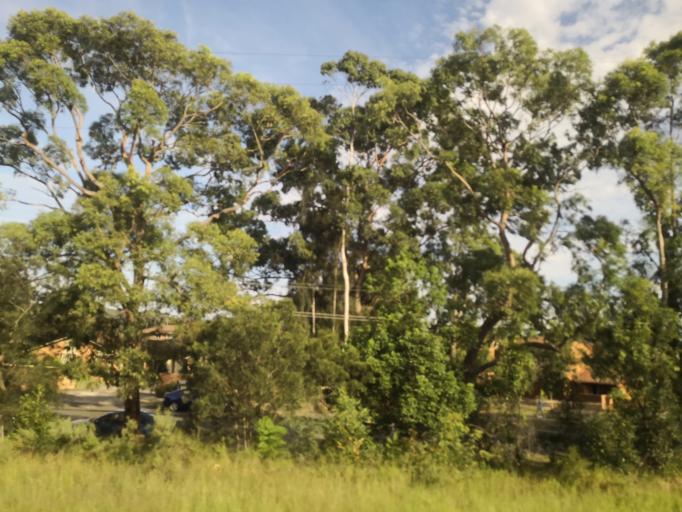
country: AU
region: New South Wales
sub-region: Gosford Shire
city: Blackwall
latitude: -33.4952
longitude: 151.3114
